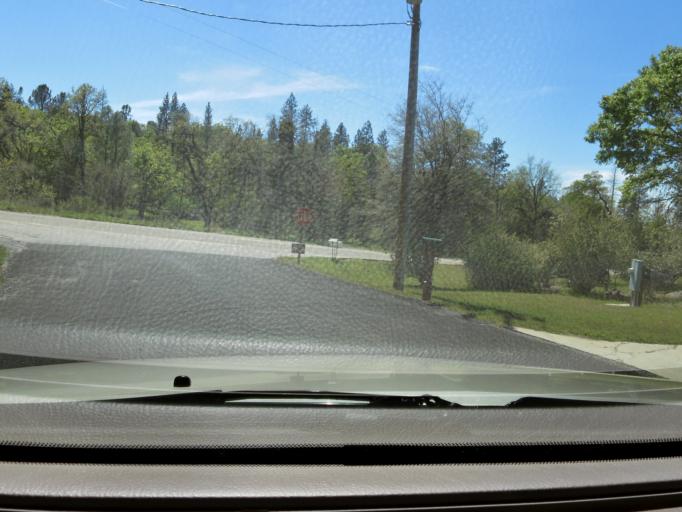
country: US
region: California
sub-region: Madera County
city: Oakhurst
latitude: 37.2879
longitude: -119.6256
